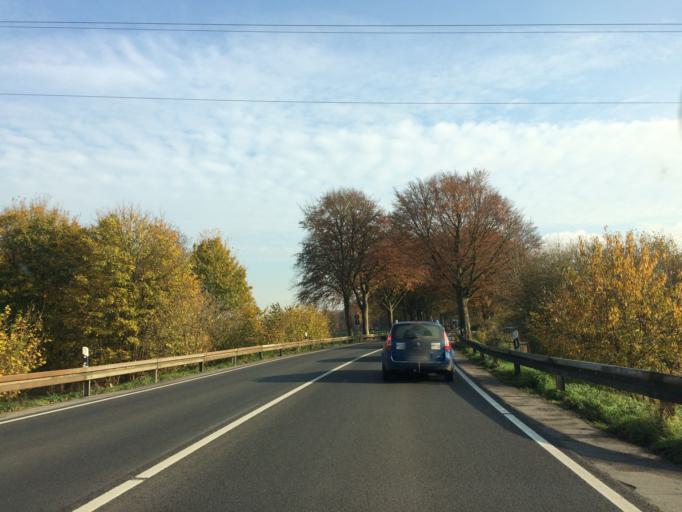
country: DE
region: North Rhine-Westphalia
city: Dorsten
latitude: 51.7238
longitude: 7.0031
